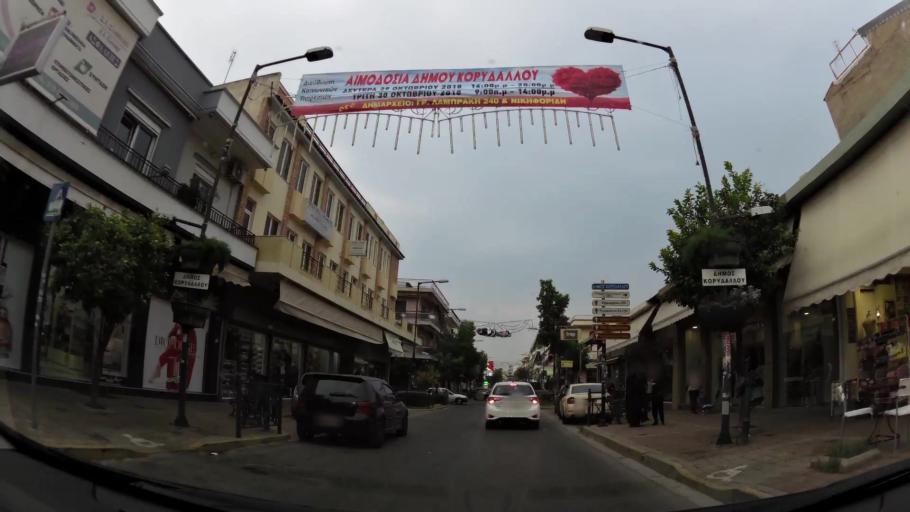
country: GR
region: Attica
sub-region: Nomarchia Athinas
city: Agia Varvara
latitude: 37.9852
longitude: 23.6573
